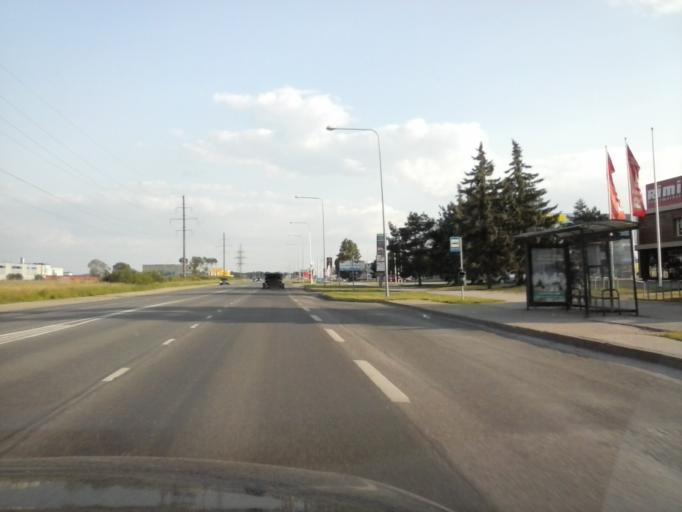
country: EE
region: Tartu
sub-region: Tartu linn
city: Tartu
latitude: 58.3497
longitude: 26.7409
